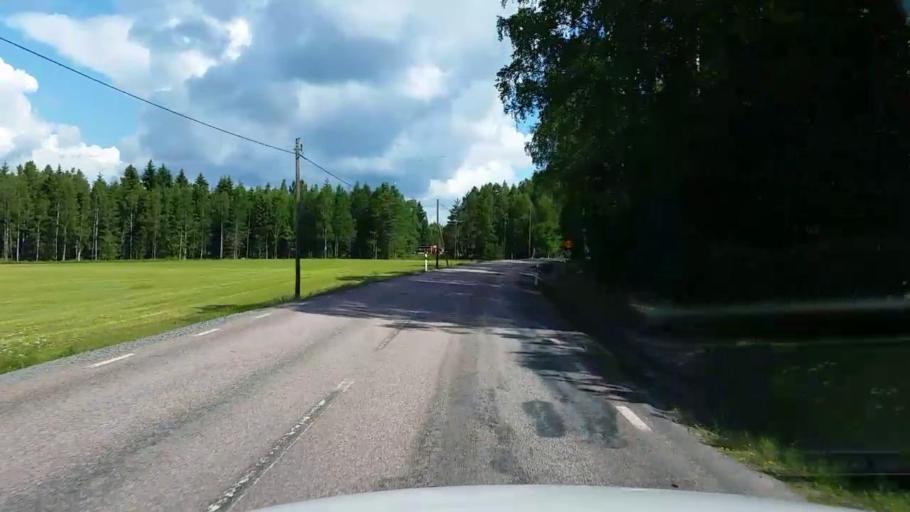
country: SE
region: Vaestmanland
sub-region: Kopings Kommun
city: Kolsva
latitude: 59.6933
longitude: 15.7750
